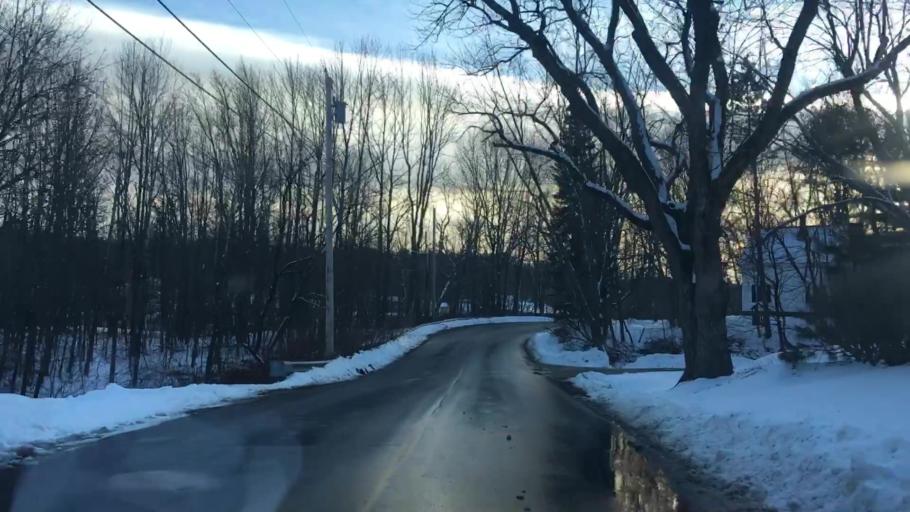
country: US
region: Maine
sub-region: Kennebec County
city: Gardiner
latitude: 44.2228
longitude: -69.7870
